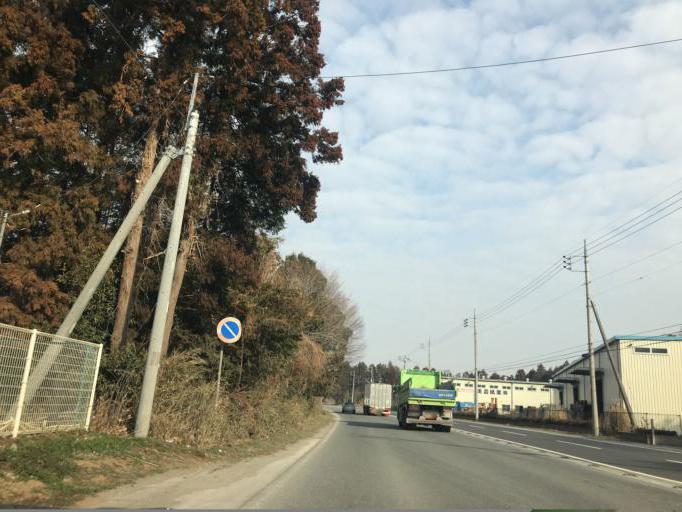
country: JP
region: Ibaraki
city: Ishige
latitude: 36.0874
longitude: 140.0388
